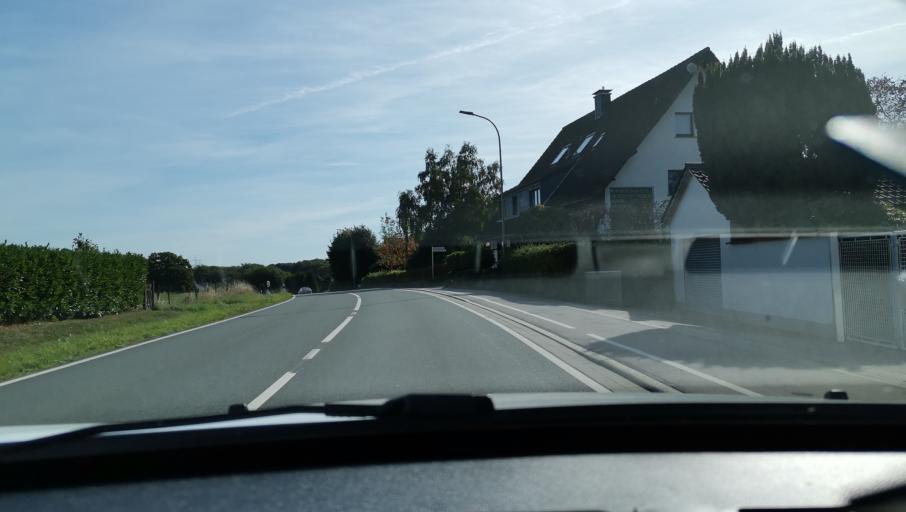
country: DE
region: North Rhine-Westphalia
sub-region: Regierungsbezirk Arnsberg
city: Breckerfeld
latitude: 51.2887
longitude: 7.4275
